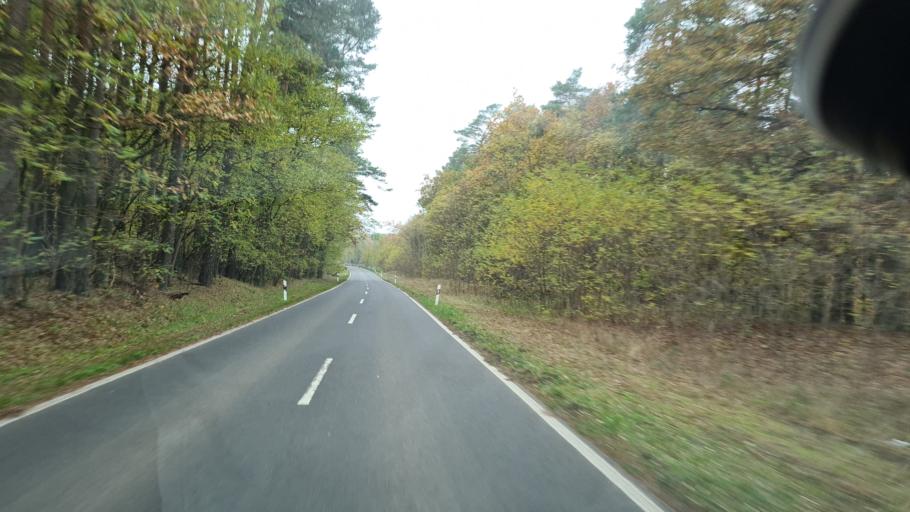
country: DE
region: Brandenburg
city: Lindow
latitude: 52.9607
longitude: 12.9994
